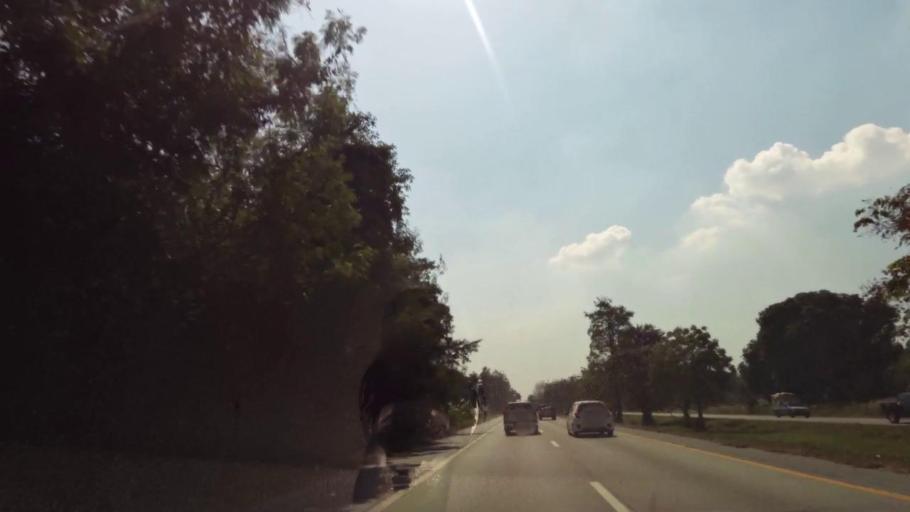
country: TH
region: Phichit
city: Wachira Barami
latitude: 16.5567
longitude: 100.1476
